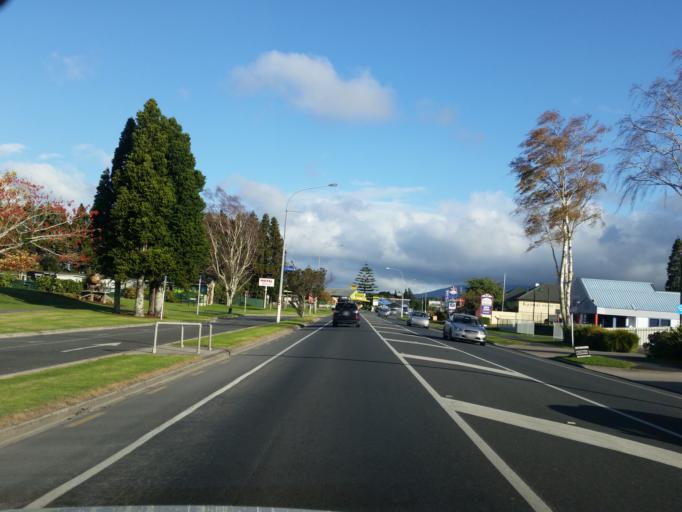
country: NZ
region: Bay of Plenty
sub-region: Western Bay of Plenty District
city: Katikati
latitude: -37.5557
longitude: 175.9169
